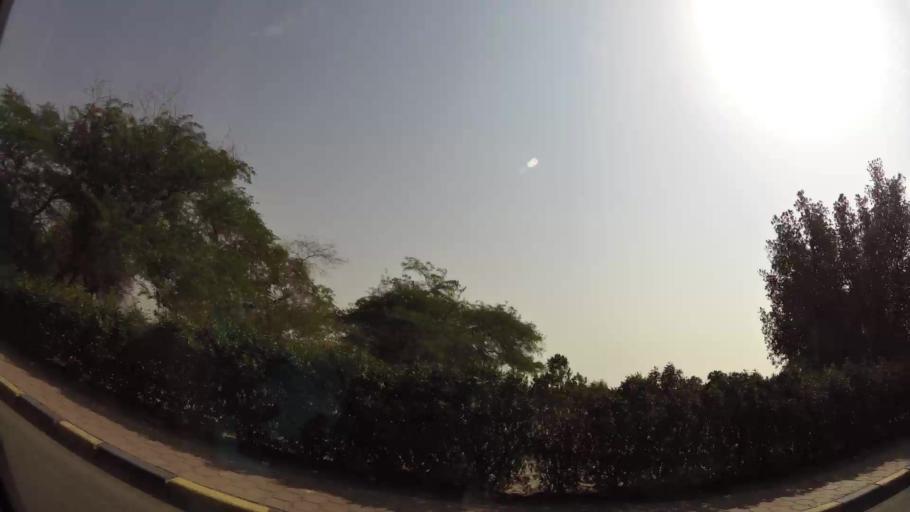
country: KW
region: Muhafazat al Jahra'
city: Al Jahra'
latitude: 29.3358
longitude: 47.6736
